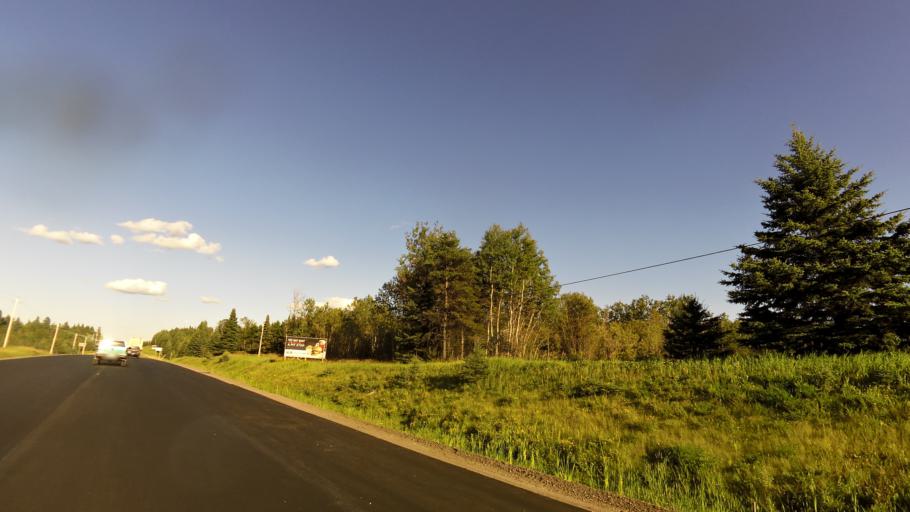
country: CA
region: Ontario
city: Dryden
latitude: 49.8151
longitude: -92.8893
